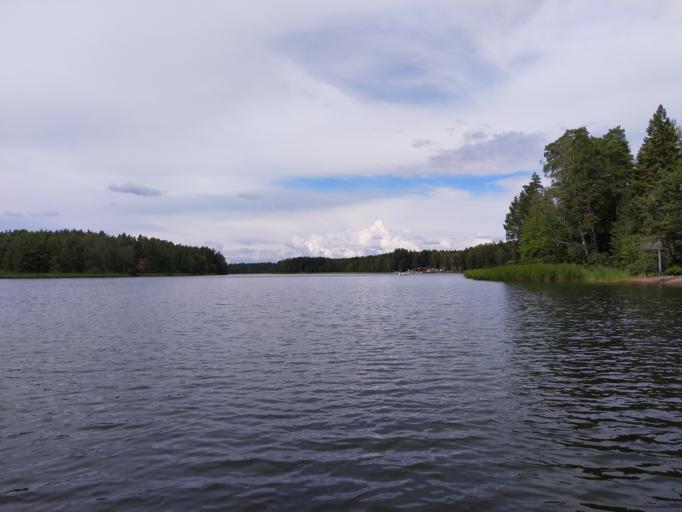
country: FI
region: Uusimaa
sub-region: Raaseporin
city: Karis
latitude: 59.9684
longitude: 23.7048
